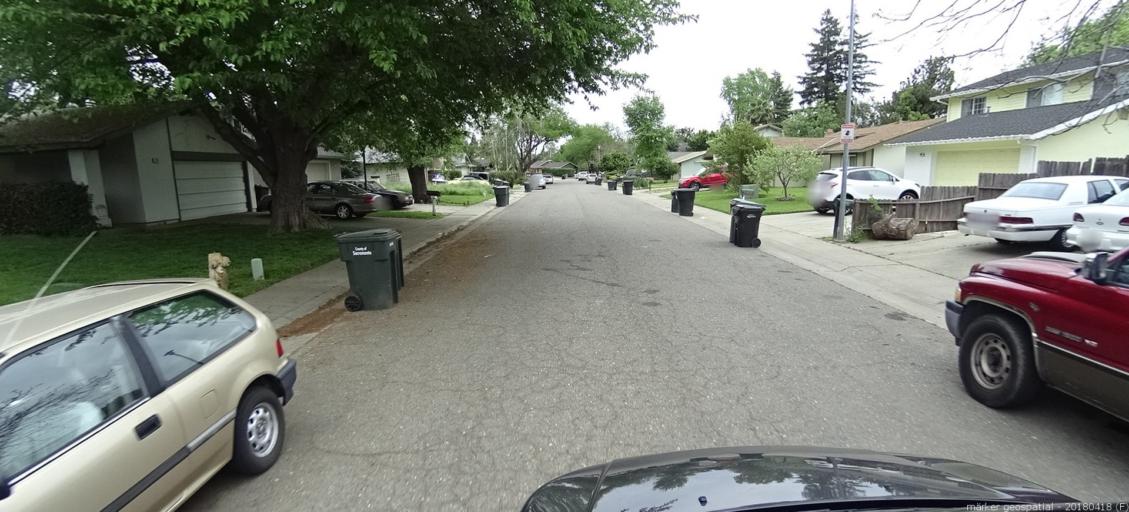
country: US
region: California
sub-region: Sacramento County
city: La Riviera
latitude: 38.5728
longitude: -121.3470
